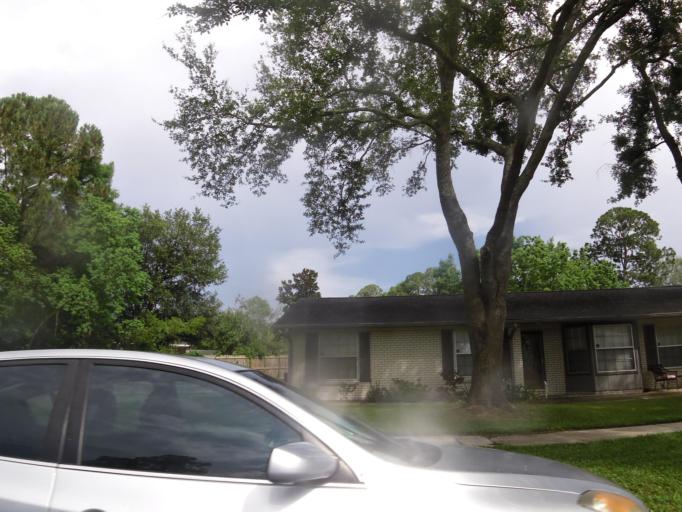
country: US
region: Florida
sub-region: Duval County
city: Jacksonville
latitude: 30.2876
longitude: -81.6063
